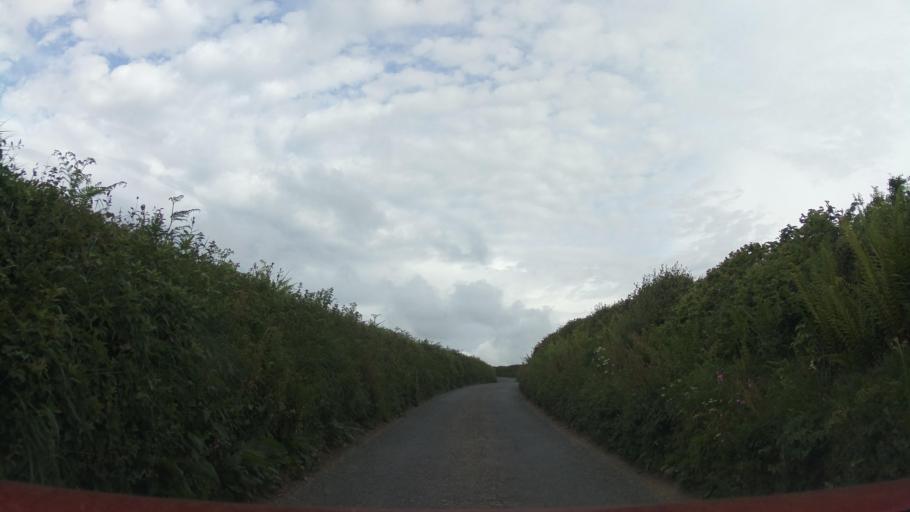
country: GB
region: England
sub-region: Devon
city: Dartmouth
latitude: 50.3272
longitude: -3.6419
